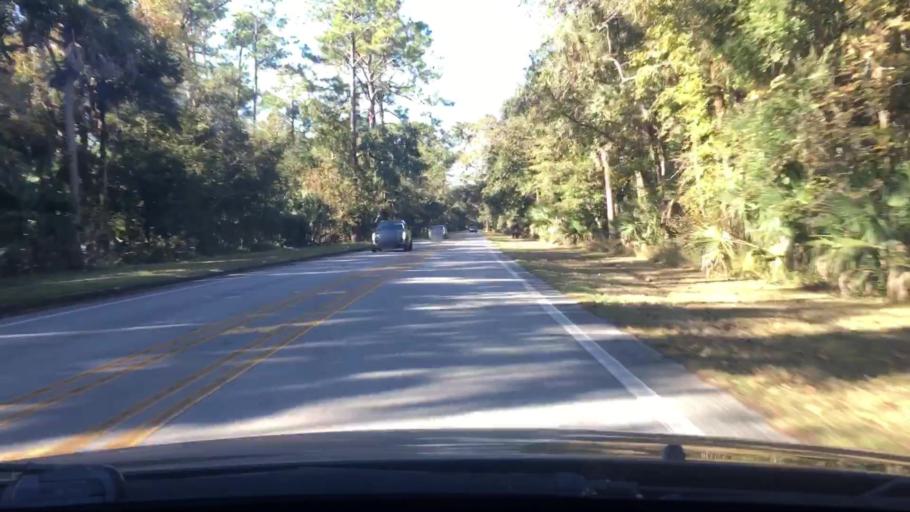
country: US
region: Florida
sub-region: Volusia County
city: Ormond-by-the-Sea
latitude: 29.3602
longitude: -81.1211
